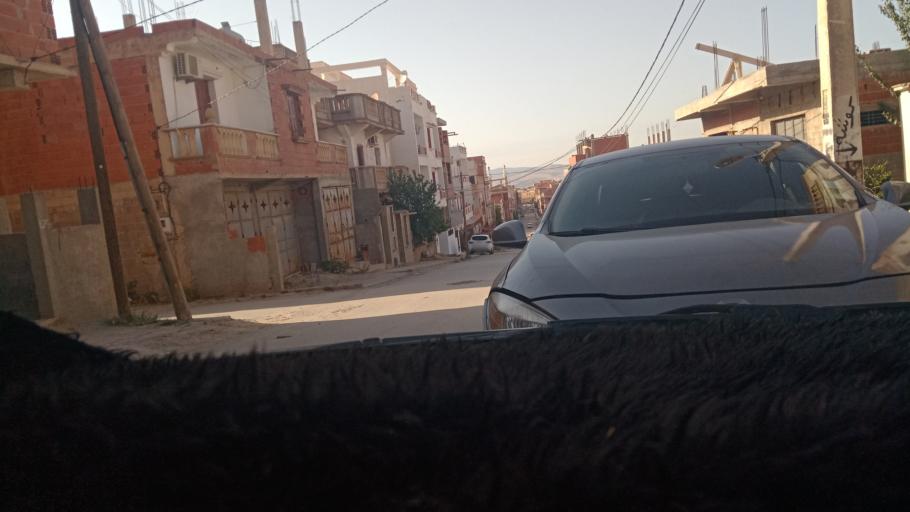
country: DZ
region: Guelma
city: Guelma
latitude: 36.4463
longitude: 7.4263
